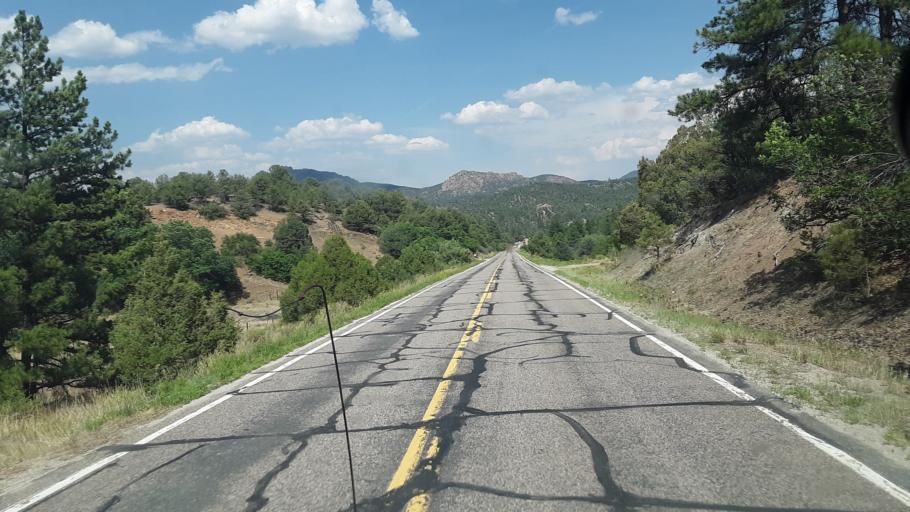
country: US
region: Colorado
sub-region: Custer County
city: Westcliffe
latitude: 38.3189
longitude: -105.6109
